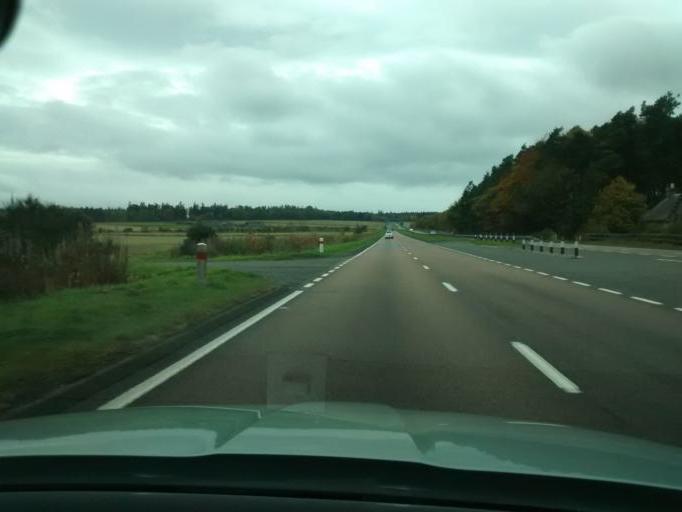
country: GB
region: Scotland
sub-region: Perth and Kinross
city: Methven
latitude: 56.3794
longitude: -3.5139
